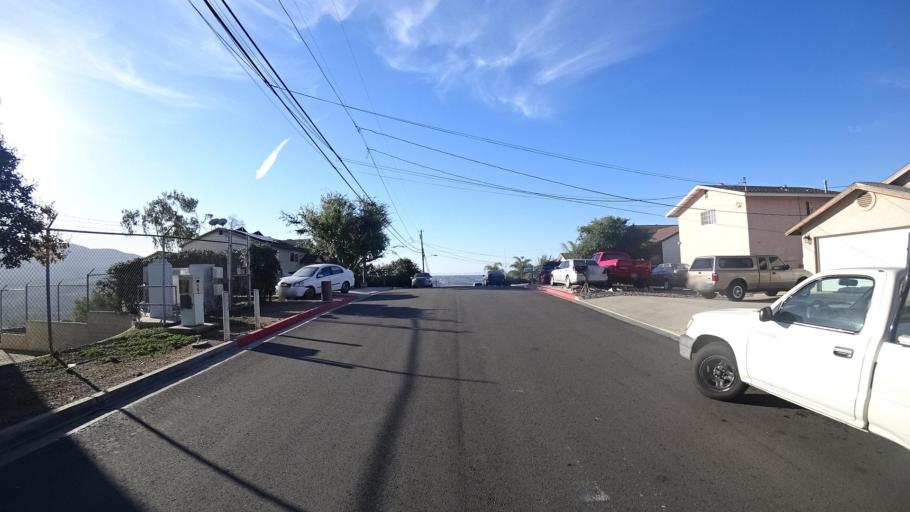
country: US
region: California
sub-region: San Diego County
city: La Presa
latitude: 32.7159
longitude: -116.9864
